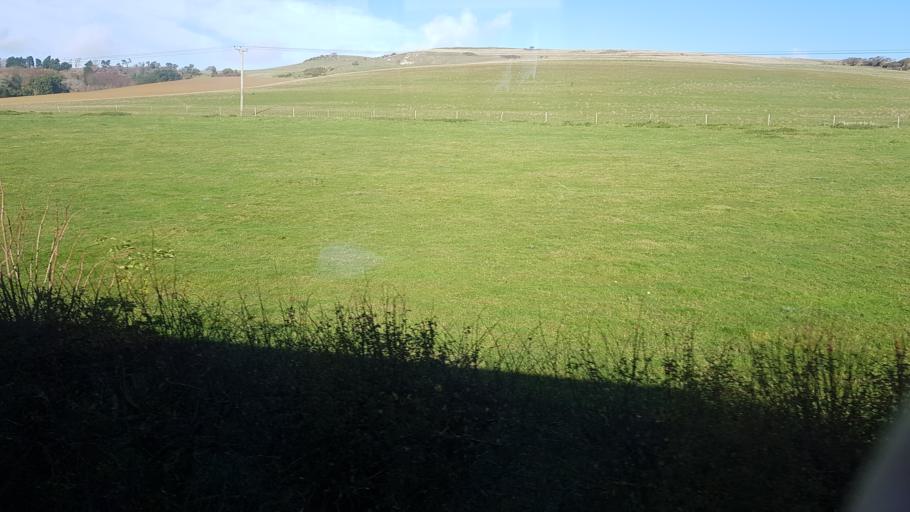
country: GB
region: England
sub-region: Isle of Wight
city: Shalfleet
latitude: 50.6422
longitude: -1.3790
